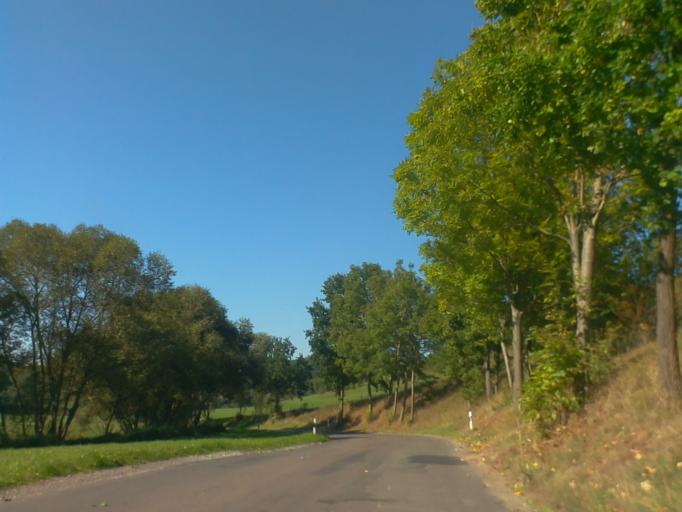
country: DE
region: Thuringia
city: Kleinebersdorf
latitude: 50.8218
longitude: 11.8295
